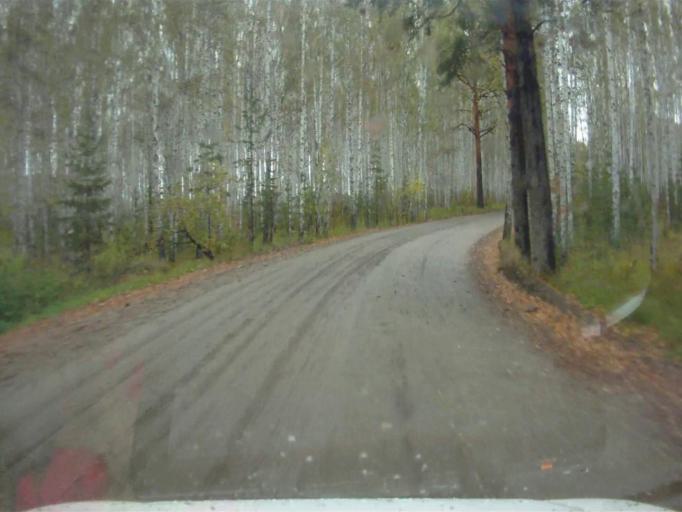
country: RU
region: Chelyabinsk
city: Kyshtym
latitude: 55.8423
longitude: 60.4857
